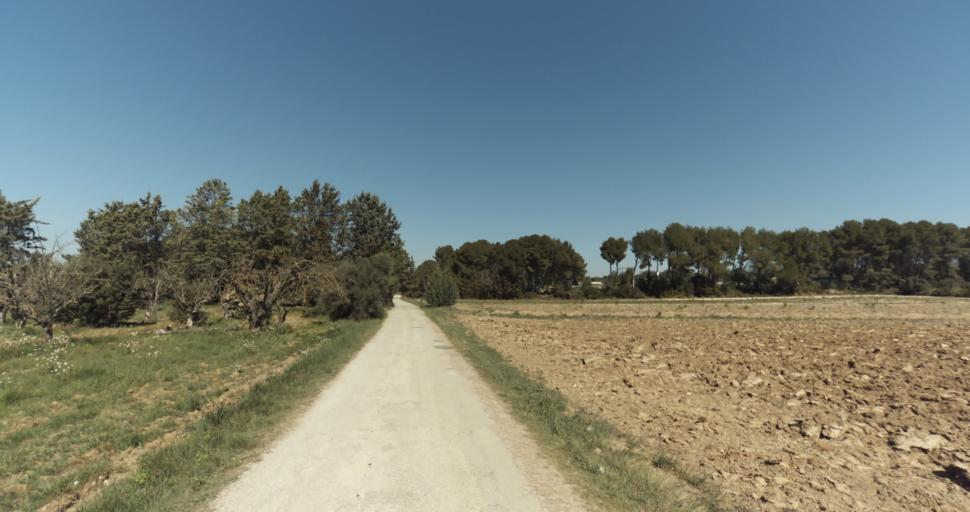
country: FR
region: Provence-Alpes-Cote d'Azur
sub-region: Departement des Bouches-du-Rhone
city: Pelissanne
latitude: 43.6121
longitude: 5.1585
